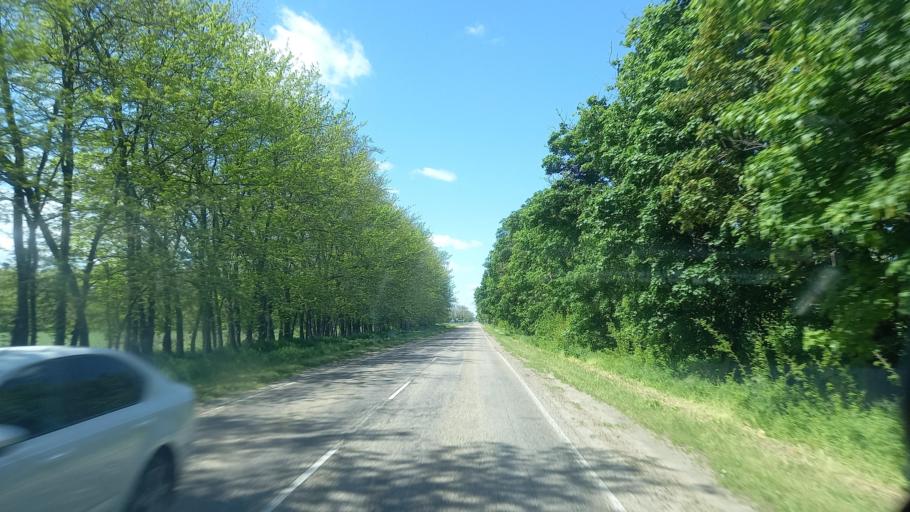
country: RU
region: Krasnodarskiy
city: Kazanskaya
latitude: 45.3683
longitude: 40.4209
